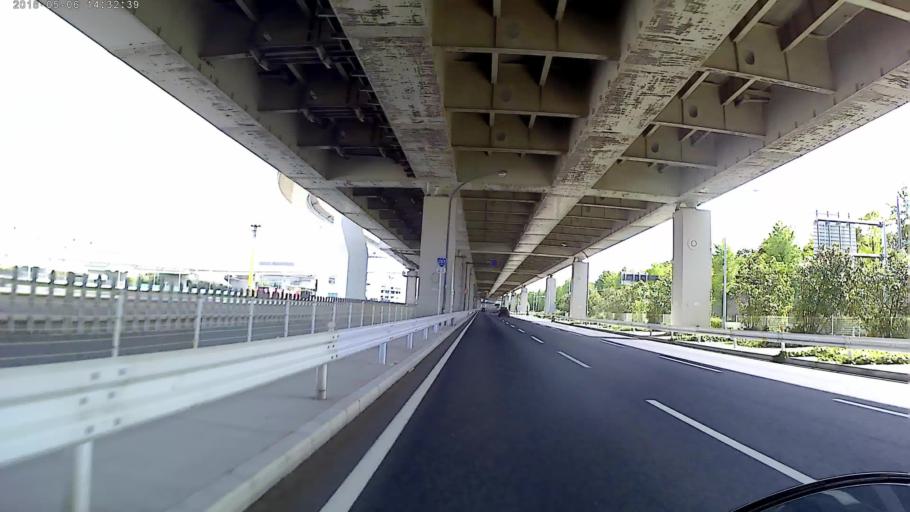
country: JP
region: Kanagawa
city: Yokohama
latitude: 35.4234
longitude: 139.6708
